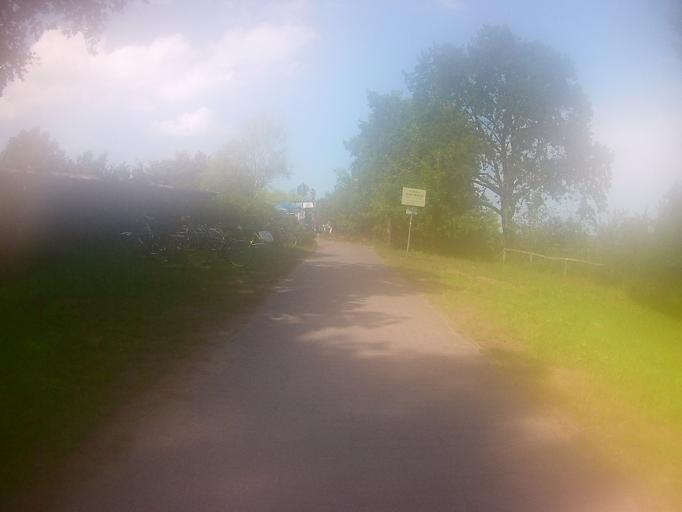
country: DE
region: Mecklenburg-Vorpommern
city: Koserow
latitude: 54.0689
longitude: 13.9669
